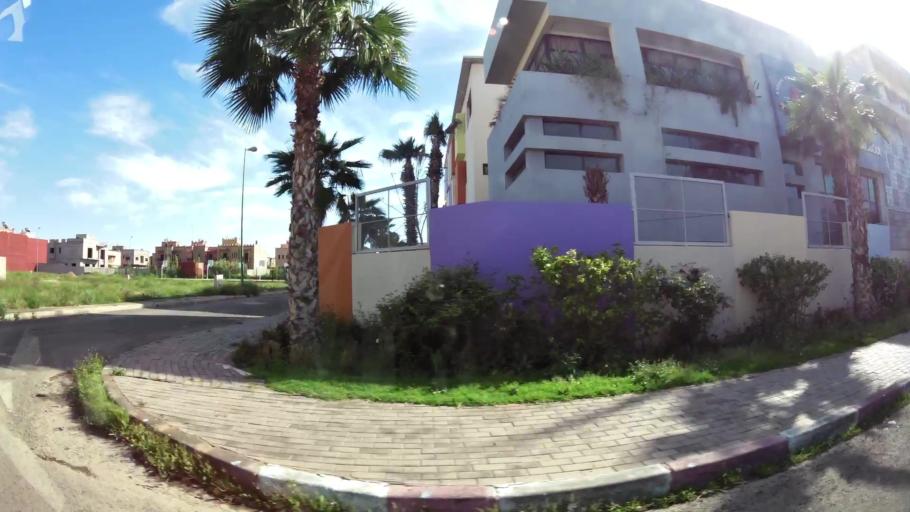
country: MA
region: Marrakech-Tensift-Al Haouz
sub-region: Marrakech
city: Marrakesh
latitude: 31.6478
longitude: -8.0421
